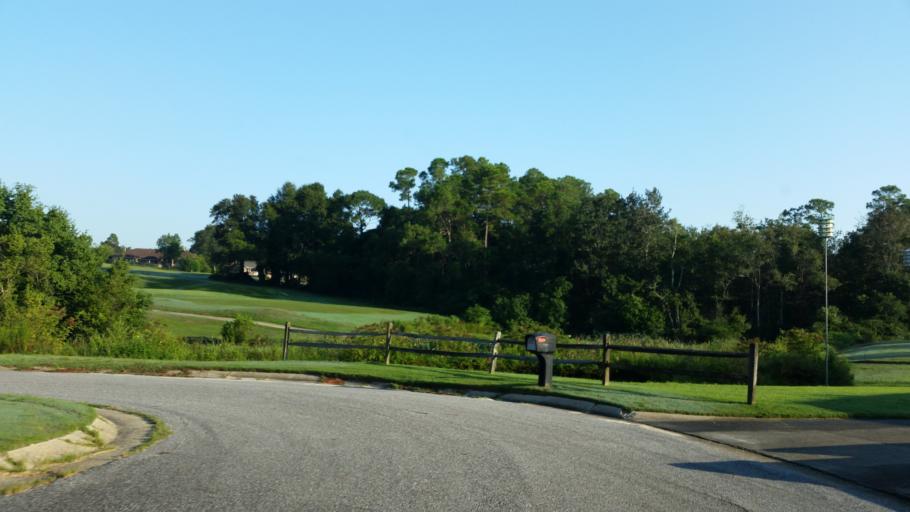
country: US
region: Florida
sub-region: Escambia County
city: Ferry Pass
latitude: 30.5420
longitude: -87.2300
